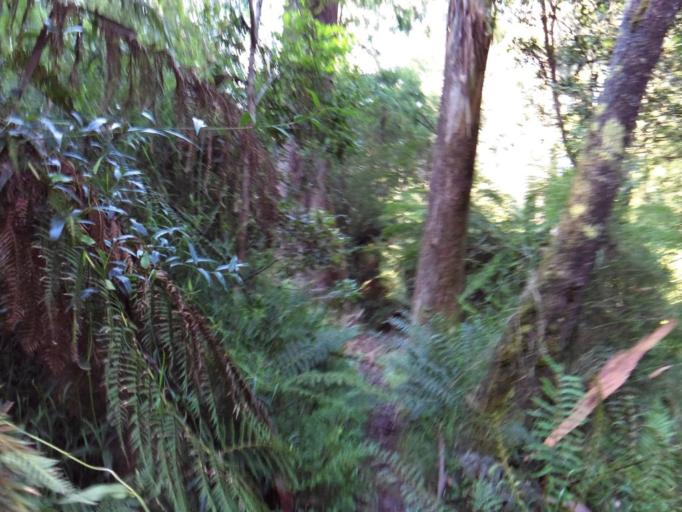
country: AU
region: Victoria
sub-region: Yarra Ranges
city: Kallista
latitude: -37.8754
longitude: 145.3670
